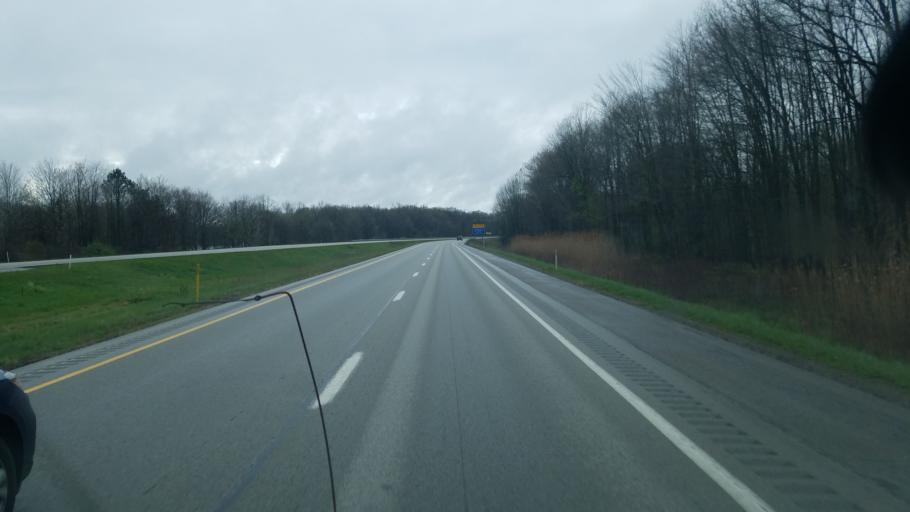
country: US
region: Pennsylvania
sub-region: Mercer County
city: Grove City
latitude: 41.1976
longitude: -80.1014
